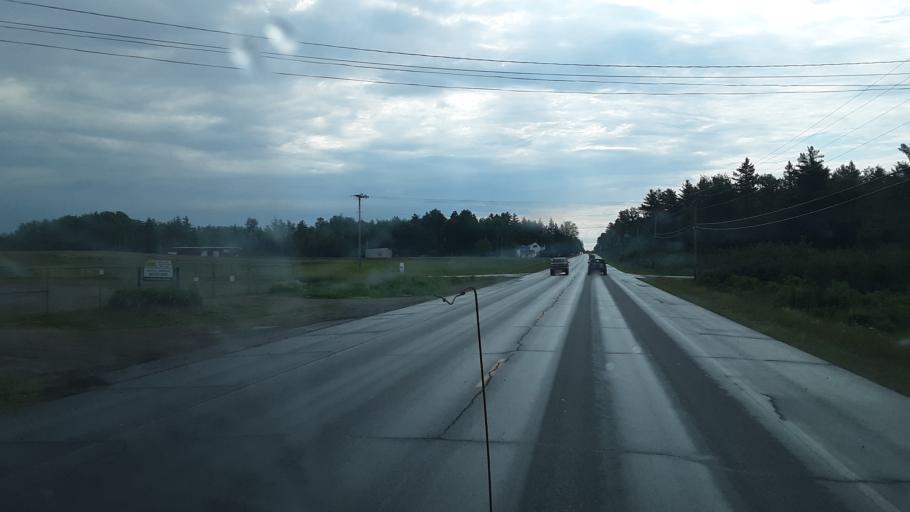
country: US
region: Maine
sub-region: Penobscot County
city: Milford
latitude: 44.9447
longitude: -68.6798
